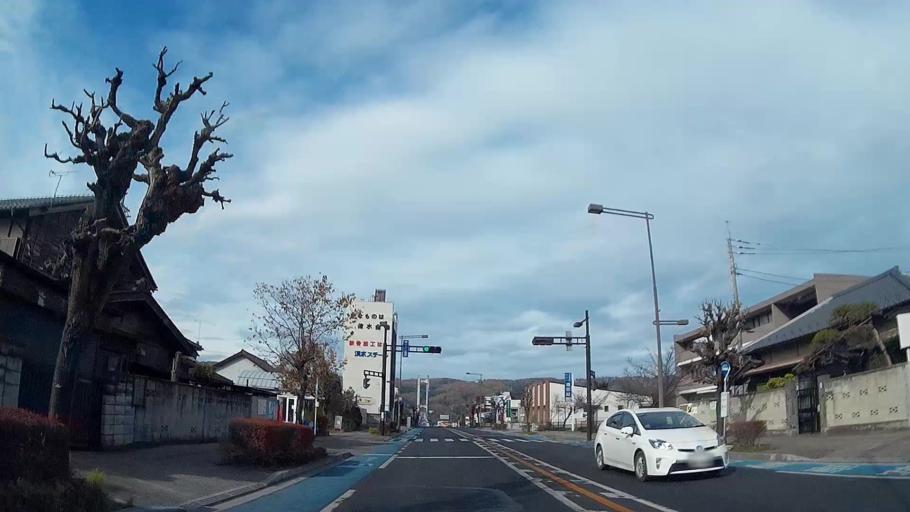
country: JP
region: Saitama
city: Chichibu
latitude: 35.9997
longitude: 139.0832
